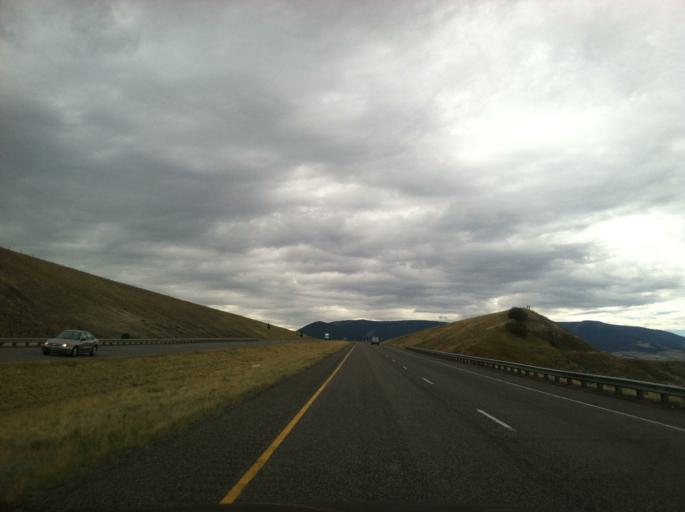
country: US
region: Montana
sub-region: Park County
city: Livingston
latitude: 45.6749
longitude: -110.5161
